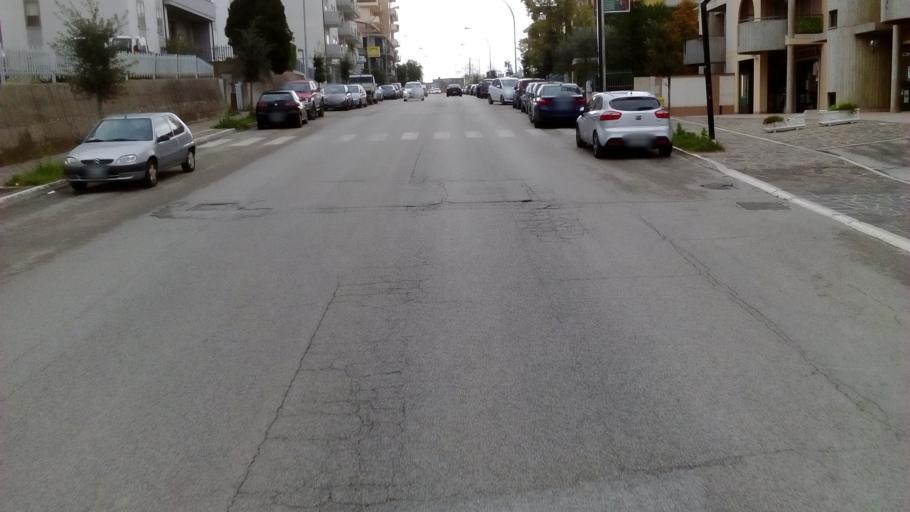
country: IT
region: Abruzzo
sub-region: Provincia di Chieti
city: Vasto
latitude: 42.1054
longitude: 14.7023
